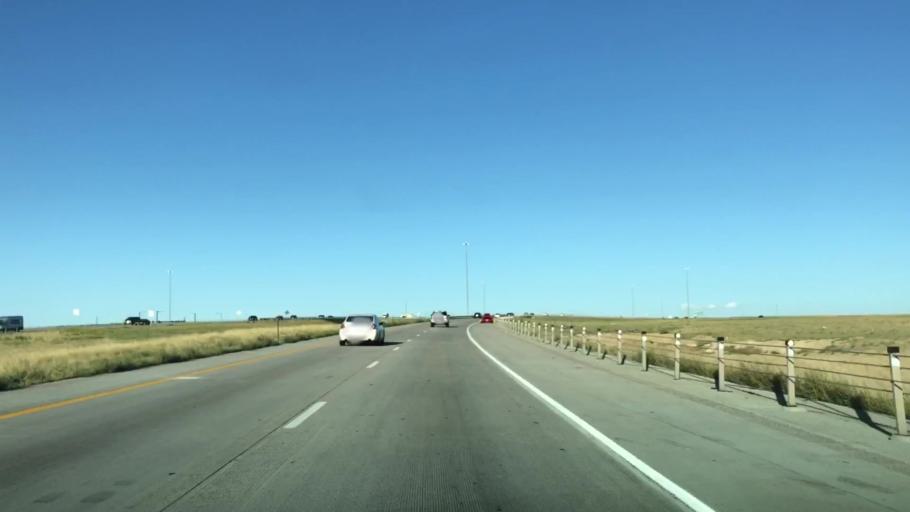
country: US
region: Colorado
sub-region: Adams County
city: Aurora
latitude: 39.8324
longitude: -104.7755
